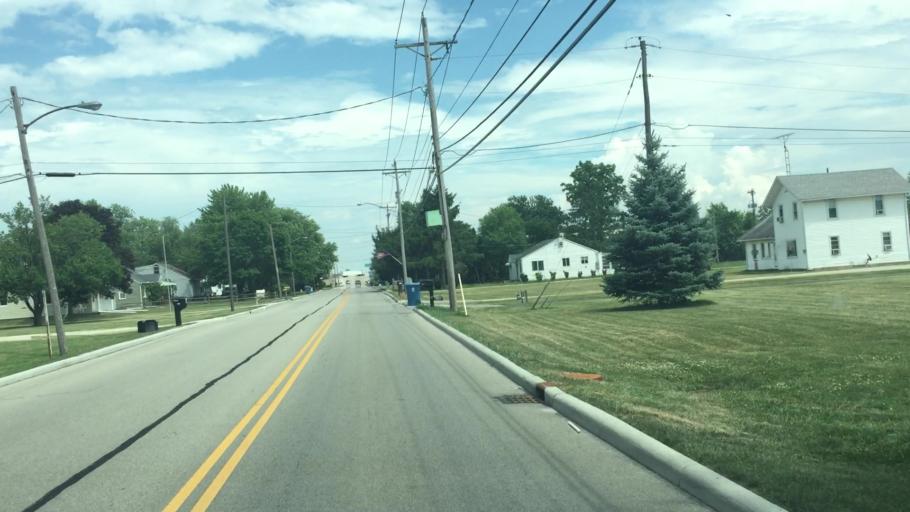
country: US
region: Ohio
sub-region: Wood County
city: Walbridge
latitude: 41.5878
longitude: -83.4856
